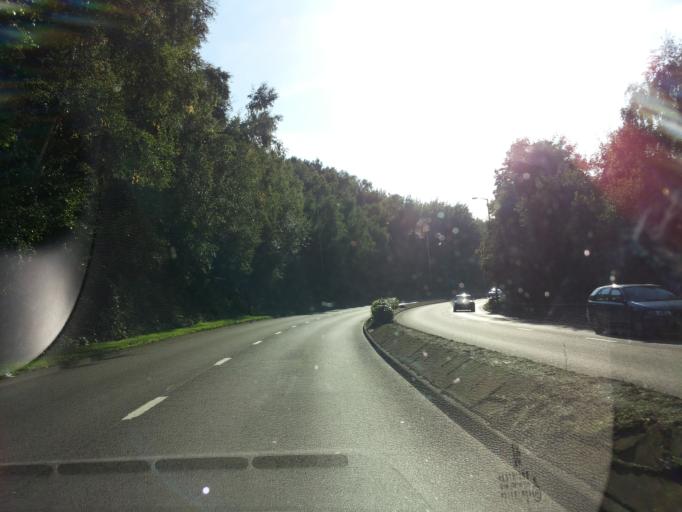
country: GB
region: England
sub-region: Worcestershire
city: Kidderminster
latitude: 52.3810
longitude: -2.2455
